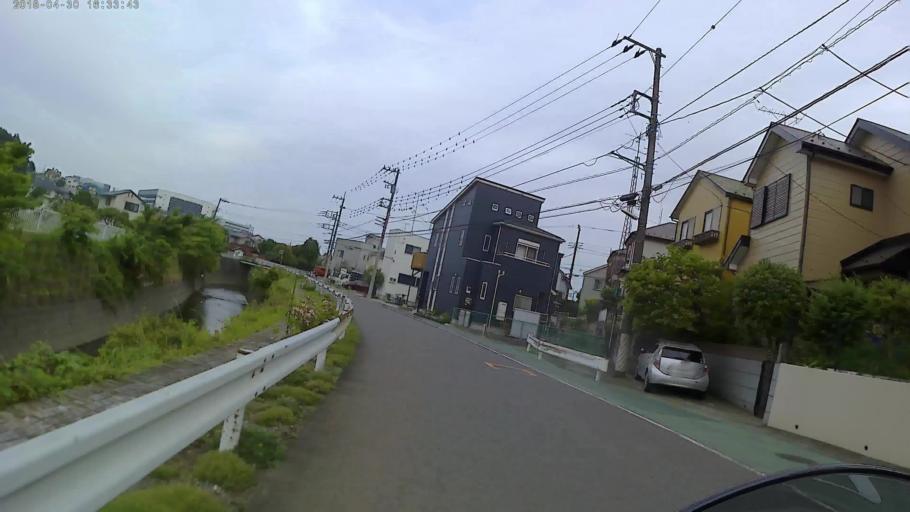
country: JP
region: Kanagawa
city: Zama
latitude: 35.4494
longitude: 139.4057
